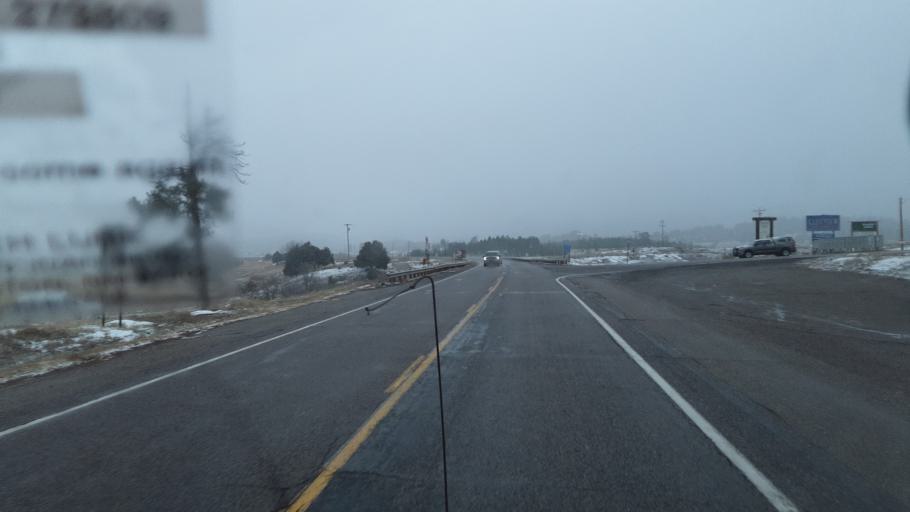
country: US
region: New Mexico
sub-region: Rio Arriba County
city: Tierra Amarilla
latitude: 36.7580
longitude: -106.5592
